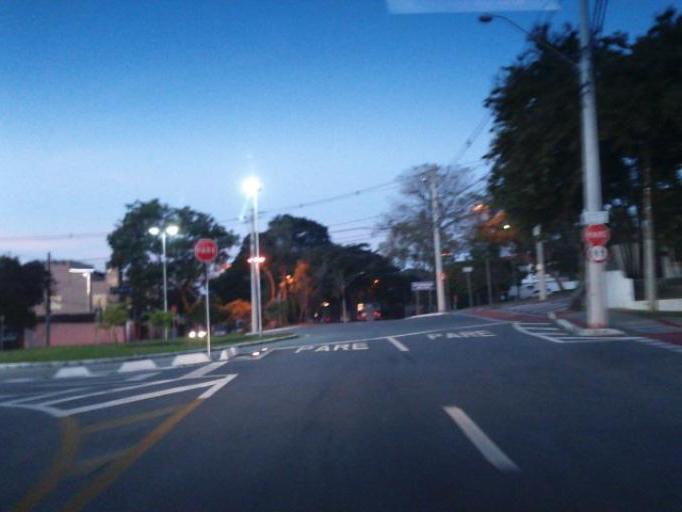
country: BR
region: Sao Paulo
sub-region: Sao Jose Dos Campos
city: Sao Jose dos Campos
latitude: -23.1959
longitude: -45.9084
